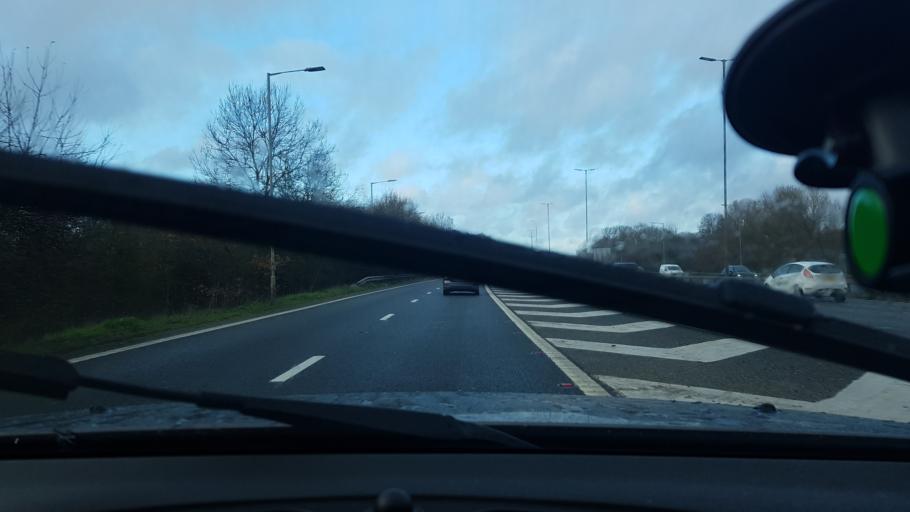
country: GB
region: England
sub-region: West Berkshire
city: Theale
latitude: 51.4413
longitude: -1.0694
